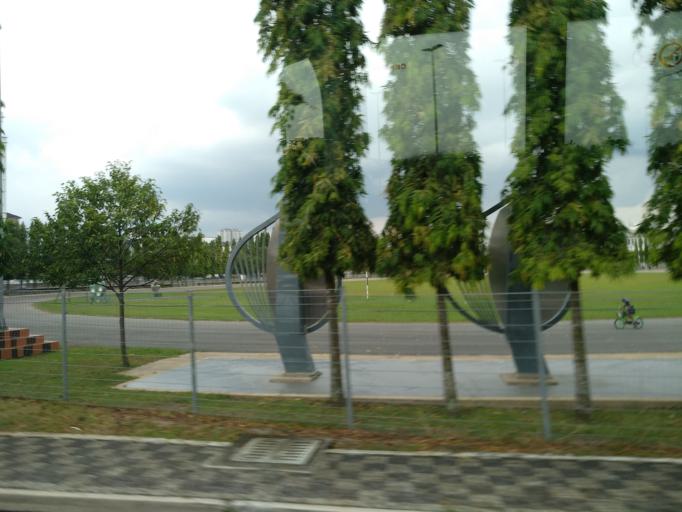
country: MY
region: Selangor
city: Kampong Baharu Balakong
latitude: 2.9955
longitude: 101.7868
